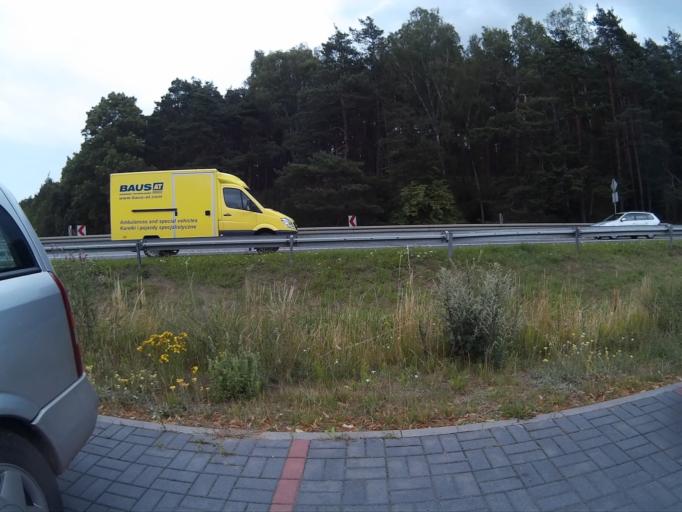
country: PL
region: Kujawsko-Pomorskie
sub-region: Powiat tucholski
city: Tuchola
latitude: 53.5625
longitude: 17.9007
